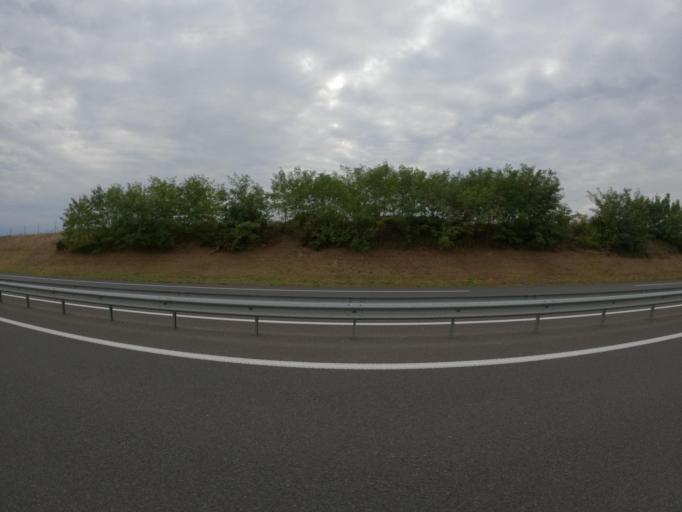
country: FR
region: Poitou-Charentes
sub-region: Departement de la Vienne
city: Terce
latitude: 46.4688
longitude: 0.5457
